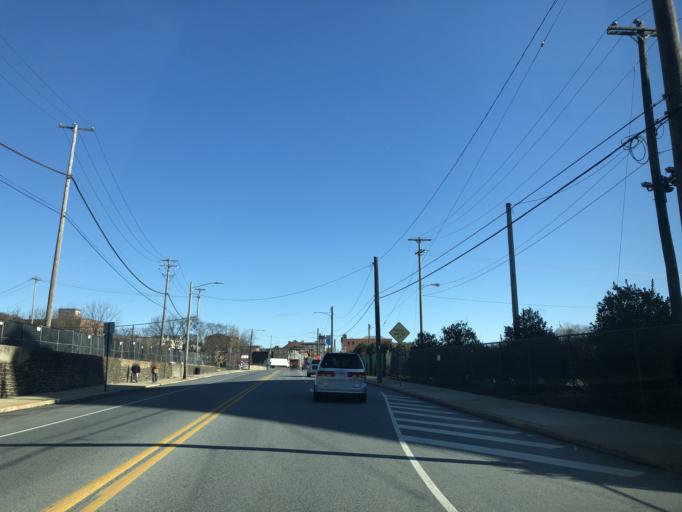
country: US
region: Pennsylvania
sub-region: Chester County
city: Coatesville
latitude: 39.9824
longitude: -75.8267
